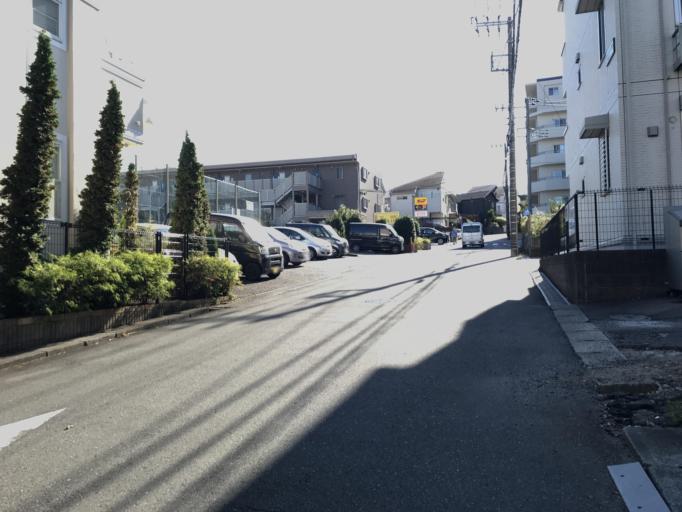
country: JP
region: Tokyo
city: Chofugaoka
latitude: 35.5701
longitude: 139.5859
